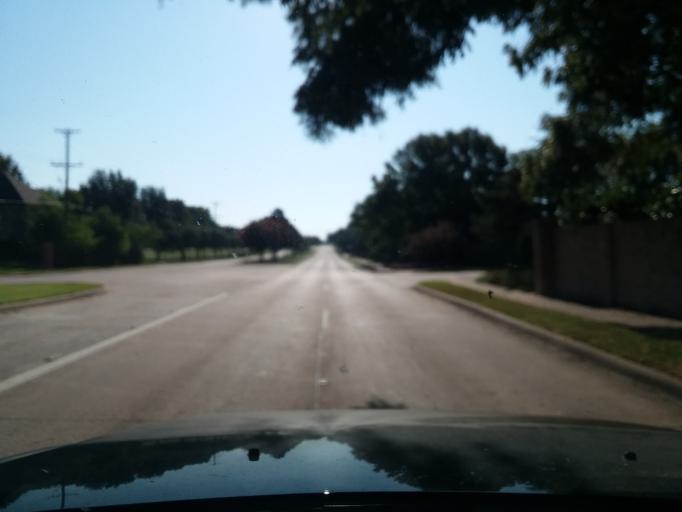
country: US
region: Texas
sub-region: Denton County
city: Highland Village
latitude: 33.0497
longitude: -97.0512
